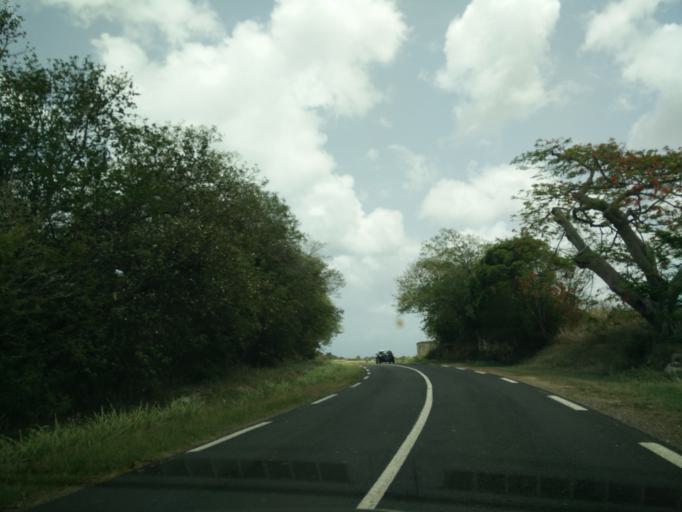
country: GP
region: Guadeloupe
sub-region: Guadeloupe
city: Port-Louis
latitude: 16.4065
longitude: -61.5076
